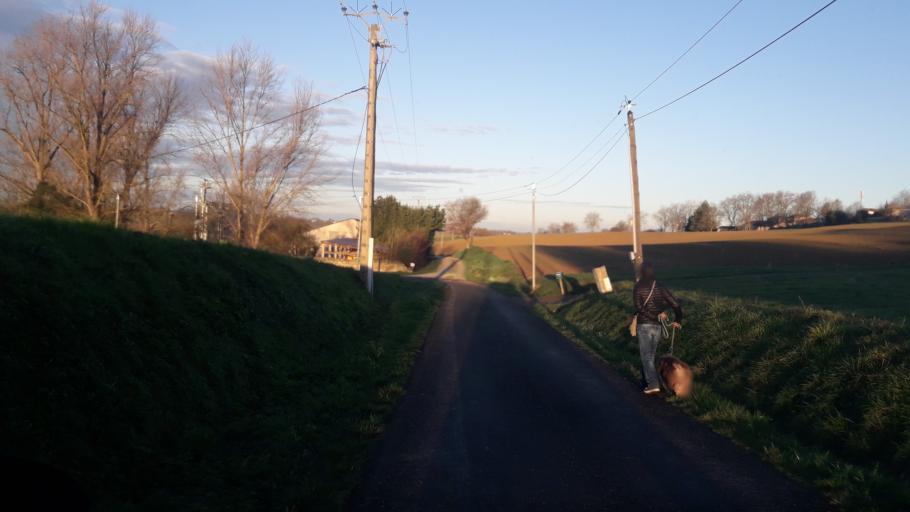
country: FR
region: Midi-Pyrenees
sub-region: Departement du Gers
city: Gimont
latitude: 43.7206
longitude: 0.9748
